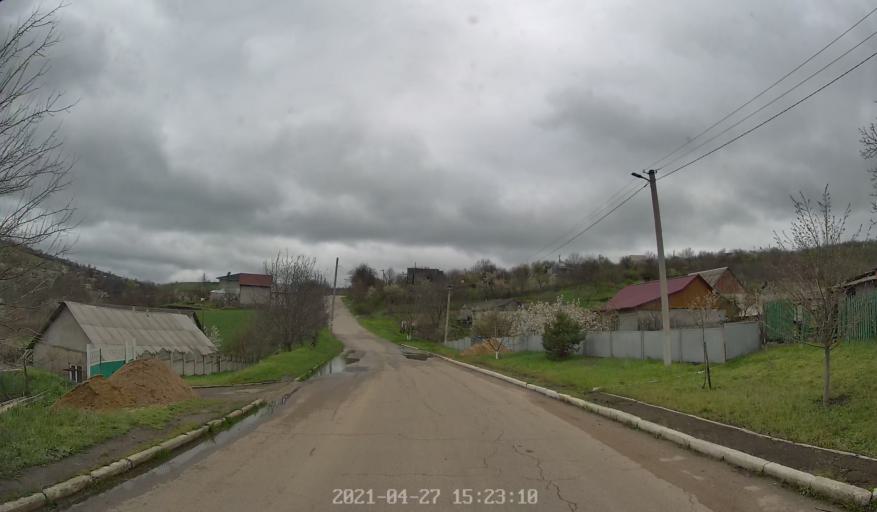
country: MD
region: Chisinau
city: Vadul lui Voda
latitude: 47.0241
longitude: 29.0246
